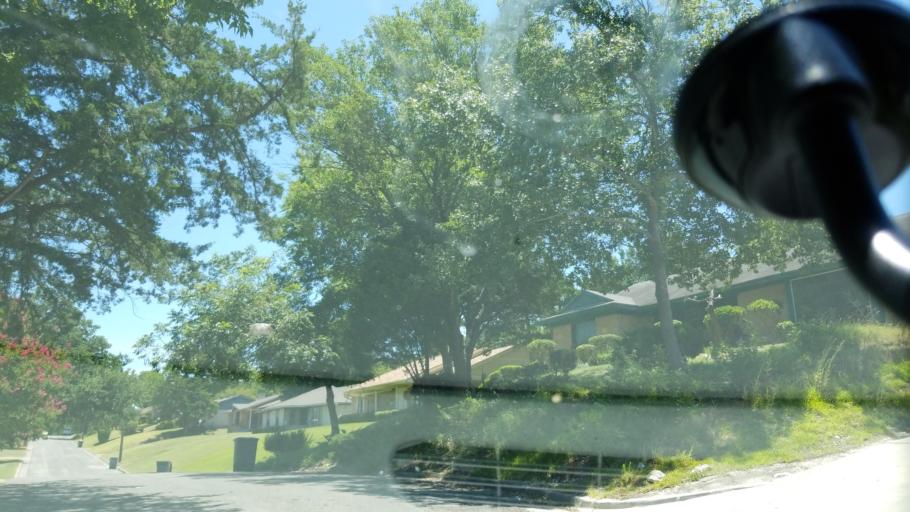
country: US
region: Texas
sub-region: Dallas County
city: Cockrell Hill
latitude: 32.6919
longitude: -96.8372
